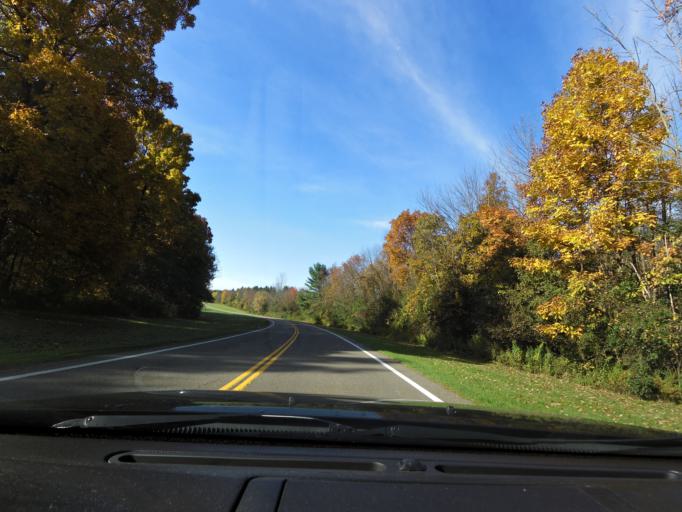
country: US
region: New York
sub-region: Livingston County
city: Mount Morris
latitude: 42.7346
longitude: -77.9124
